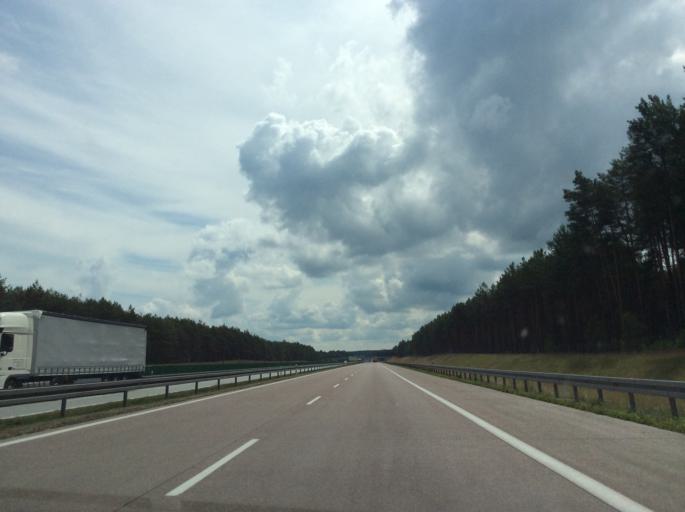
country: PL
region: Lubusz
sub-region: Powiat slubicki
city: Rzepin
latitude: 52.3342
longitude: 14.8089
